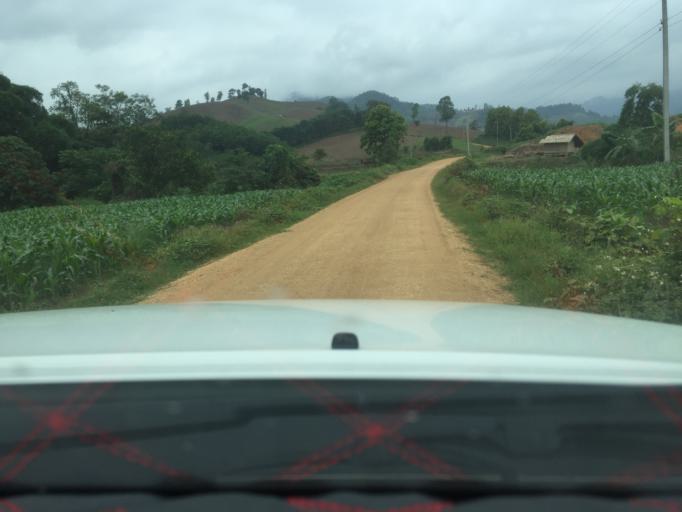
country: TH
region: Phayao
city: Phu Sang
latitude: 19.6978
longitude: 100.4955
